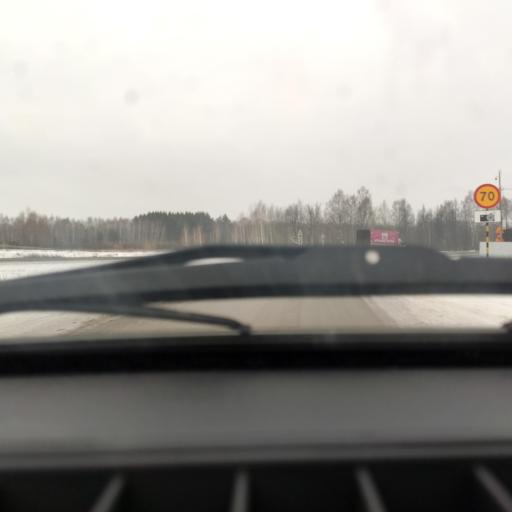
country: RU
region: Bashkortostan
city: Iglino
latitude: 54.7425
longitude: 56.3018
